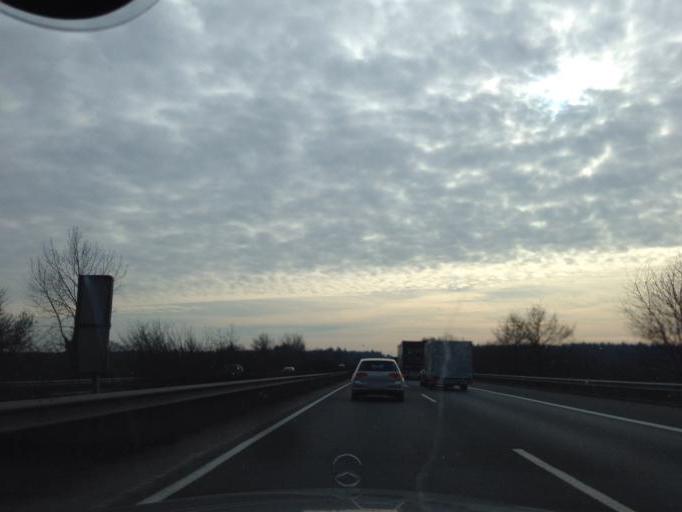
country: DE
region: Lower Saxony
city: Holdorf
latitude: 52.5554
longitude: 8.1136
